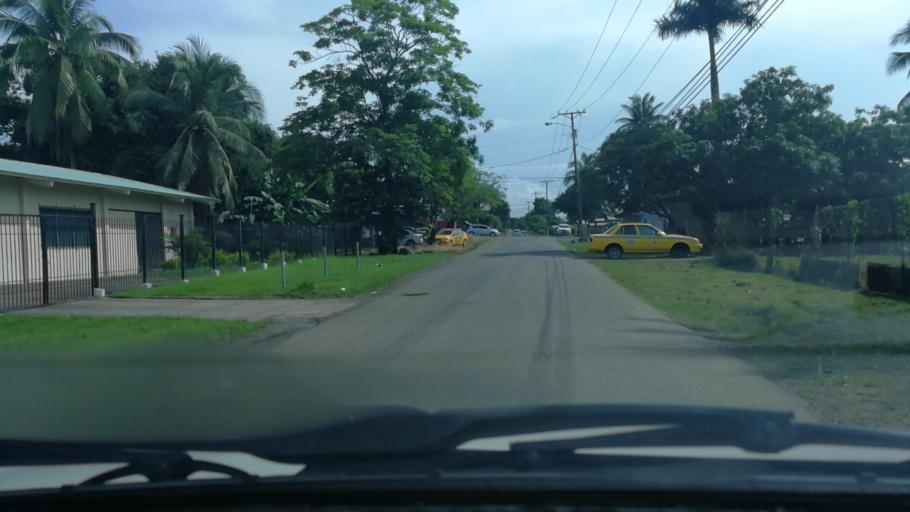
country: PA
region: Panama
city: Pacora
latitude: 9.0802
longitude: -79.2945
